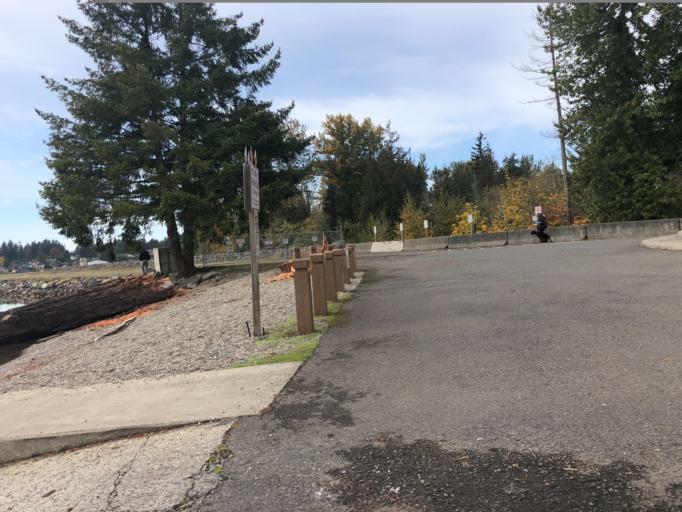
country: US
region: Washington
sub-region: Pierce County
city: Bonney Lake
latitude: 47.2409
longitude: -122.1690
